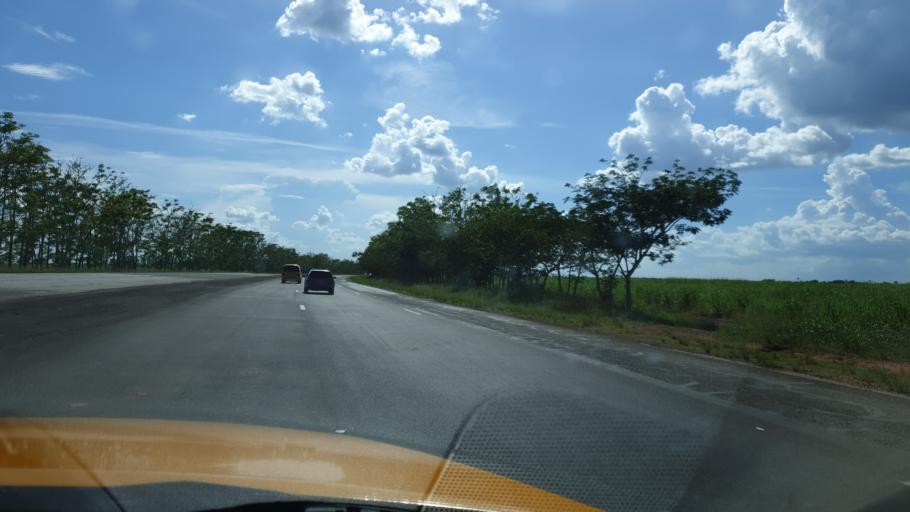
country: CU
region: Cienfuegos
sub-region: Municipio de Aguada de Pasajeros
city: Aguada de Pasajeros
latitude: 22.4021
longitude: -80.8530
